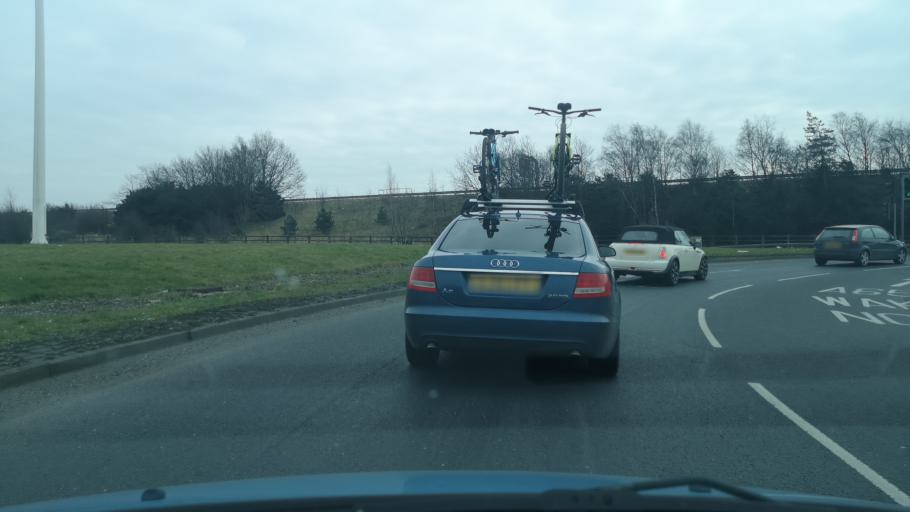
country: GB
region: England
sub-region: City and Borough of Wakefield
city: Normanton
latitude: 53.7095
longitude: -1.3946
